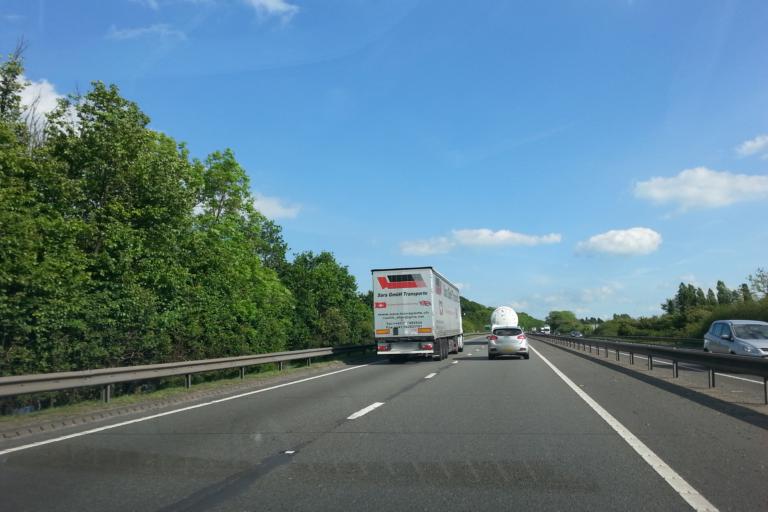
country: GB
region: England
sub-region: Nottinghamshire
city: Newark on Trent
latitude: 53.0874
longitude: -0.7793
